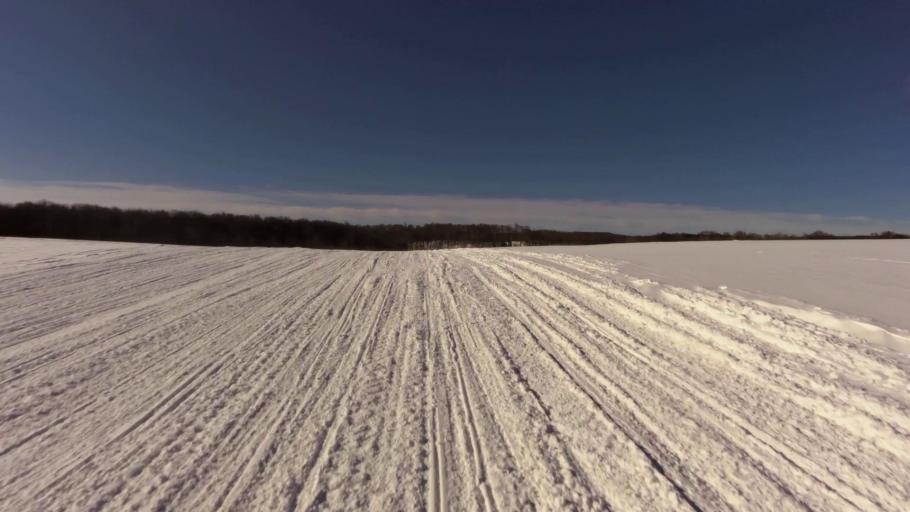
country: US
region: New York
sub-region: Cattaraugus County
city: Franklinville
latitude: 42.3944
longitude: -78.4742
